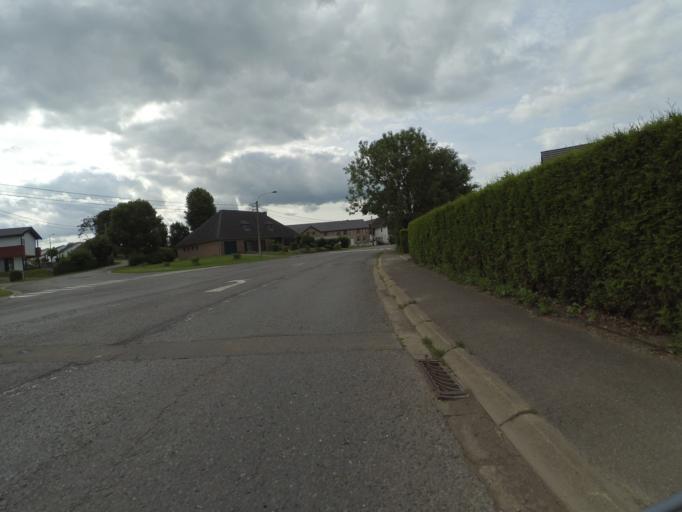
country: BE
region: Wallonia
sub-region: Province de Liege
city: Lontzen
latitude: 50.6820
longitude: 6.0372
